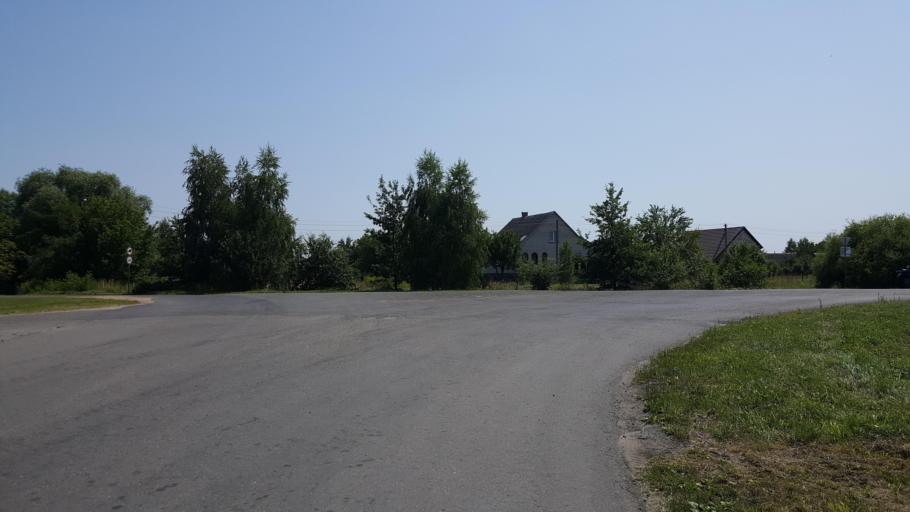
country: BY
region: Brest
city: Zhabinka
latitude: 52.1880
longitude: 23.9960
